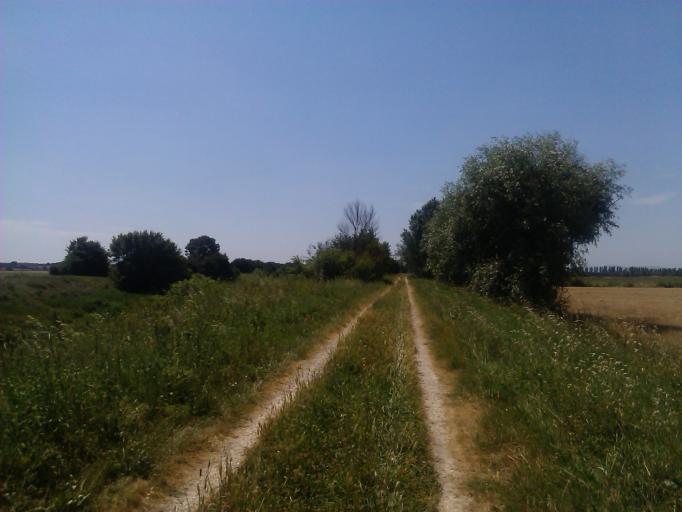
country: IT
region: Tuscany
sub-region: Province of Arezzo
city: Cesa
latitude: 43.3392
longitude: 11.8282
